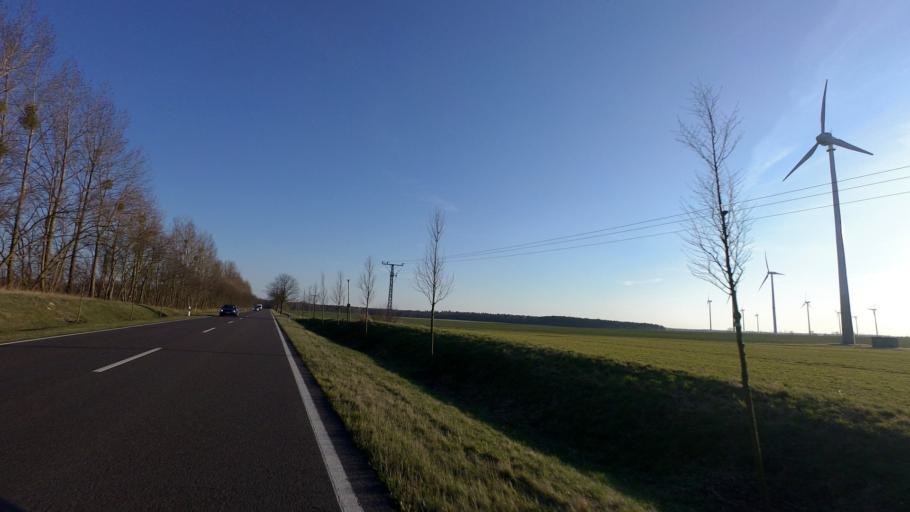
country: DE
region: Brandenburg
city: Werftpfuhl
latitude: 52.6917
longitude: 13.8361
